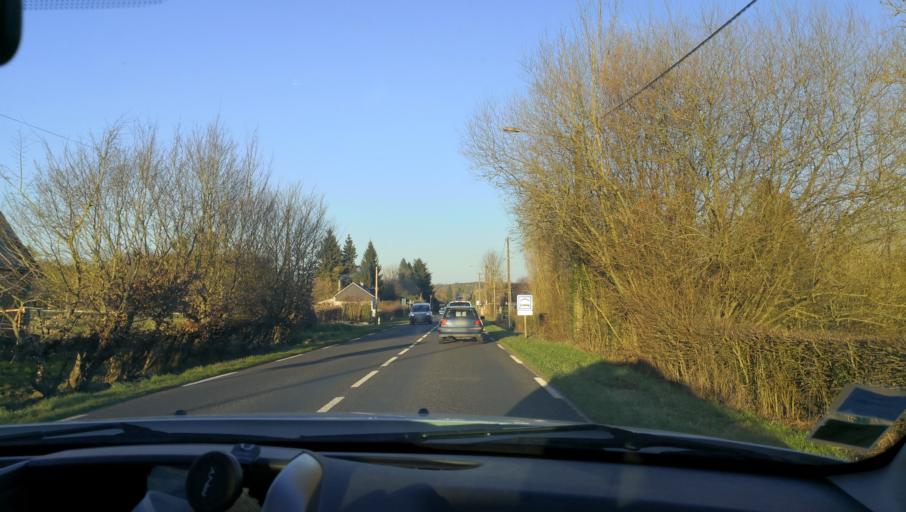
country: FR
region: Haute-Normandie
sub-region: Departement de la Seine-Maritime
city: Forges-les-Eaux
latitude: 49.6018
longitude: 1.4800
